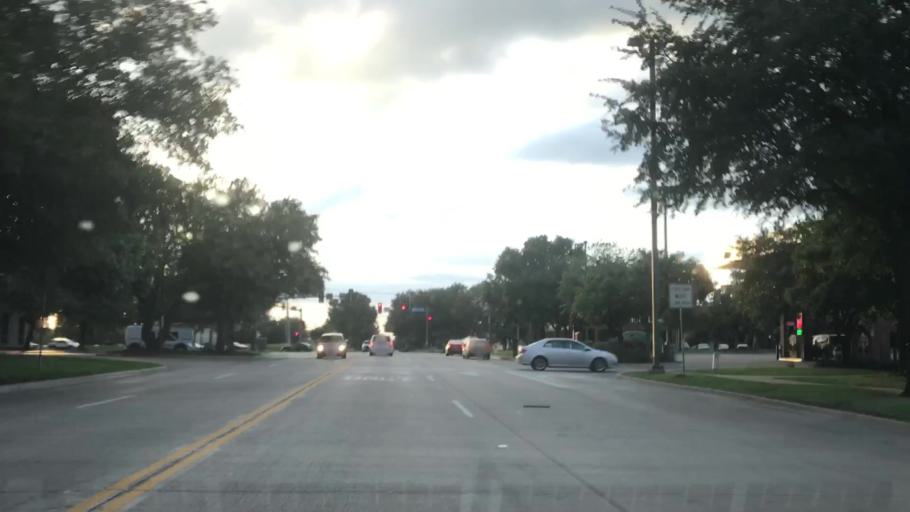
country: US
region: Texas
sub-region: Dallas County
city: Addison
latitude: 32.9562
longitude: -96.8534
